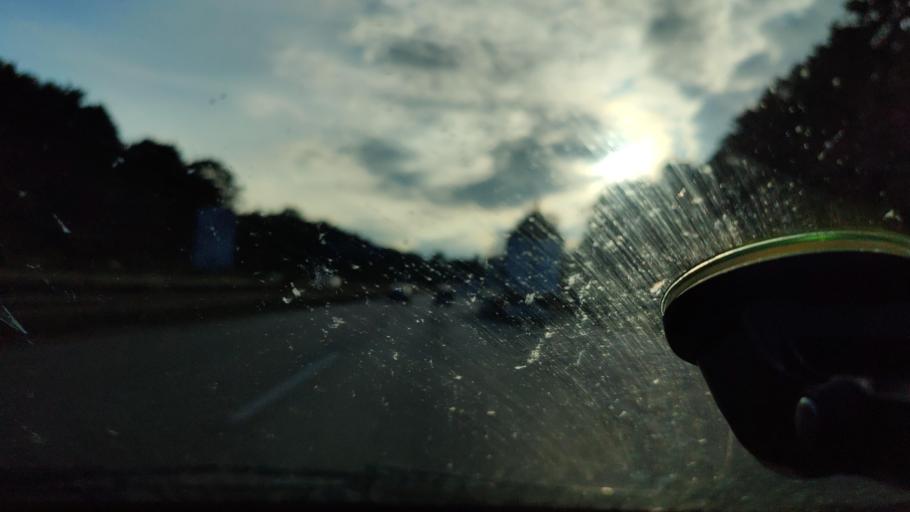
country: DE
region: North Rhine-Westphalia
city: Meiderich
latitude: 51.4855
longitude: 6.8026
